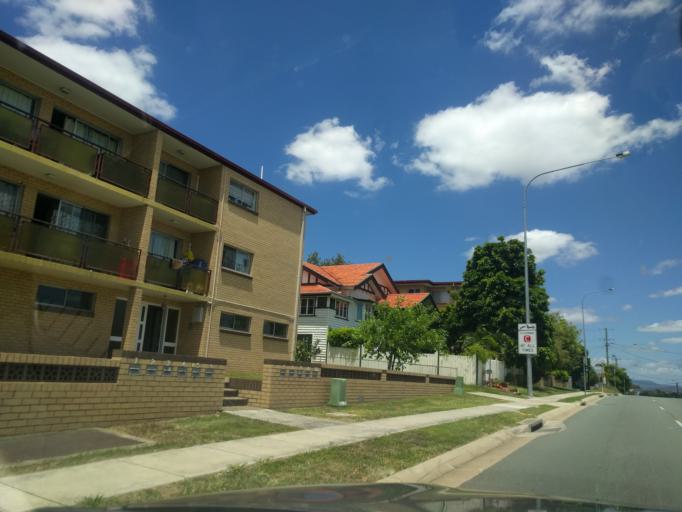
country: AU
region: Queensland
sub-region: Brisbane
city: Gordon Park
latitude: -27.4119
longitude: 153.0272
